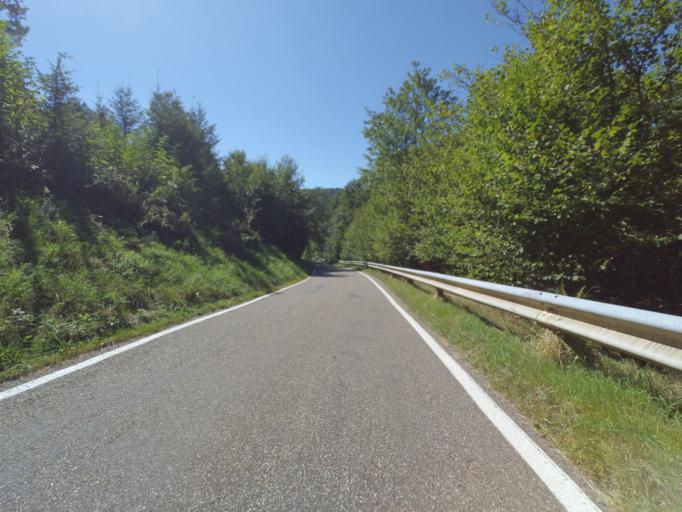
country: DE
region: Rheinland-Pfalz
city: Bad Bertrich
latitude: 50.0688
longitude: 7.0258
